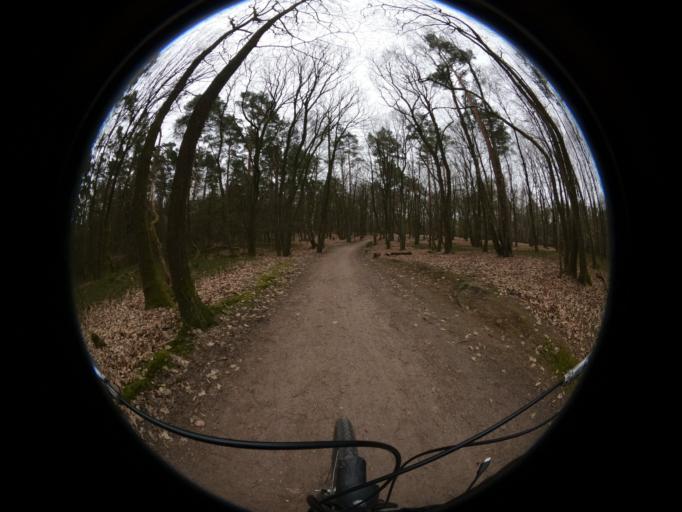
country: DE
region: Lower Saxony
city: Neu Wulmstorf
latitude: 53.4483
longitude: 9.8519
